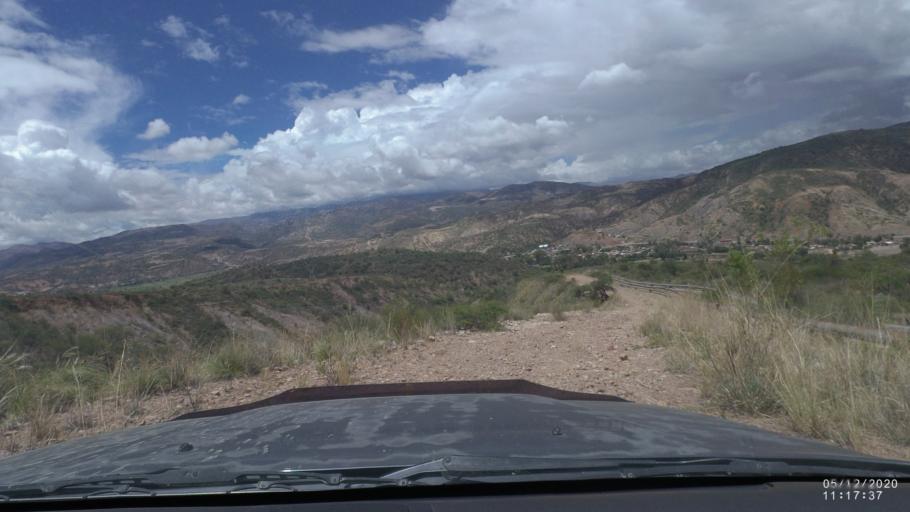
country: BO
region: Cochabamba
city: Sipe Sipe
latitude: -17.5522
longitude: -66.3312
